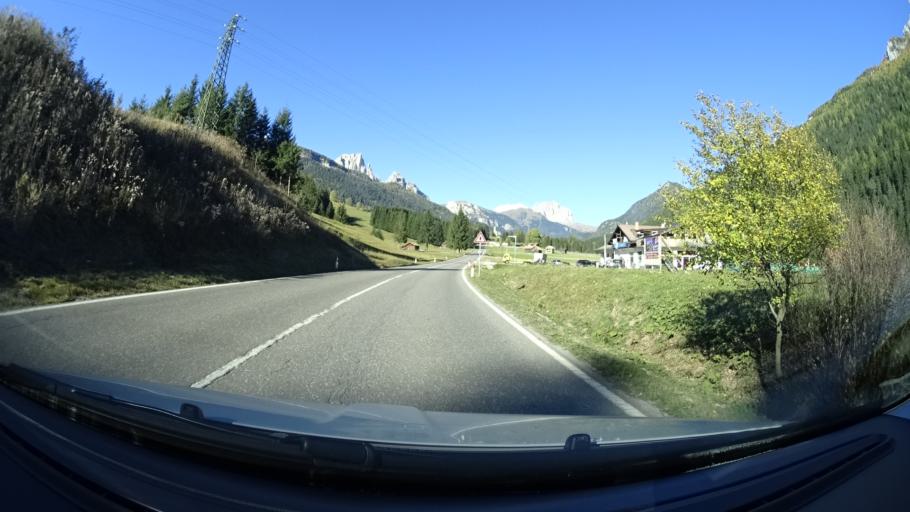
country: IT
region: Trentino-Alto Adige
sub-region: Provincia di Trento
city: Vigo di Fassa
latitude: 46.4088
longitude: 11.6764
